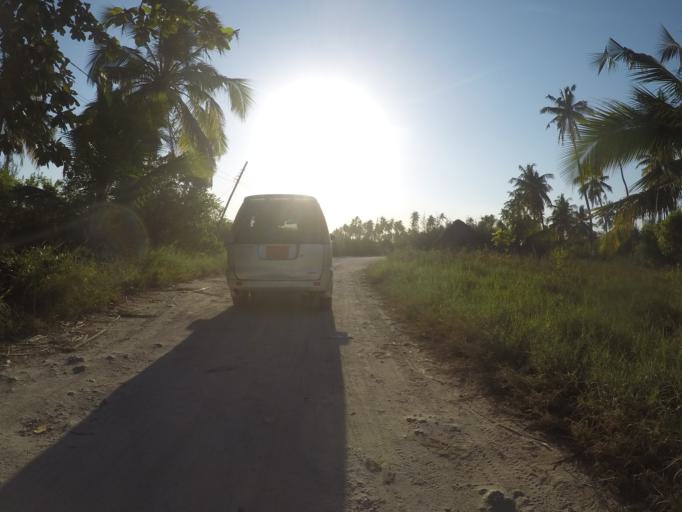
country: TZ
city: Kiwengwa
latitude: -6.1444
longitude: 39.4947
